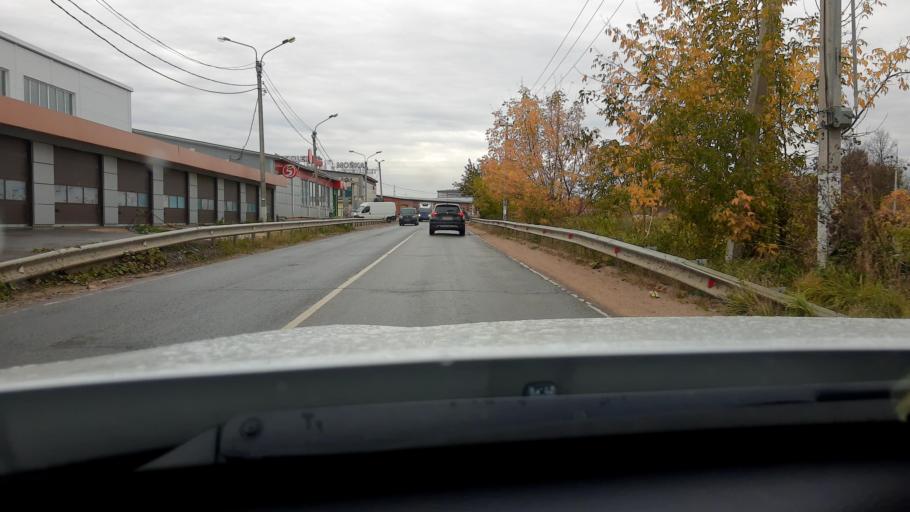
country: RU
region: Moskovskaya
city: Domodedovo
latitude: 55.4300
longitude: 37.7152
